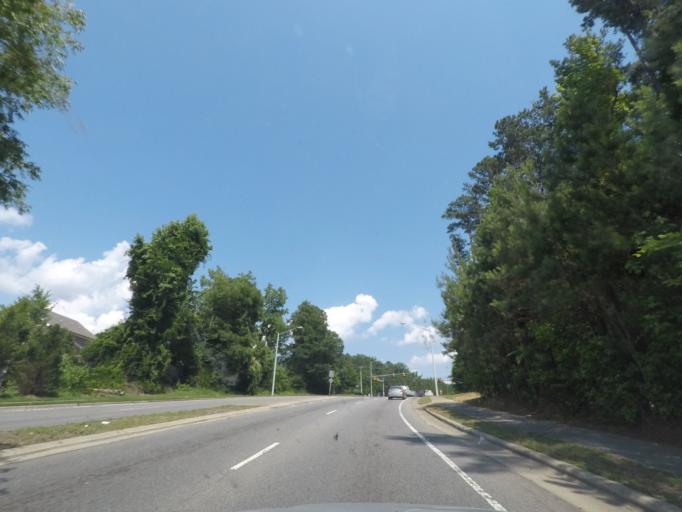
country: US
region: North Carolina
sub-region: Durham County
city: Durham
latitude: 35.9581
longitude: -78.9354
